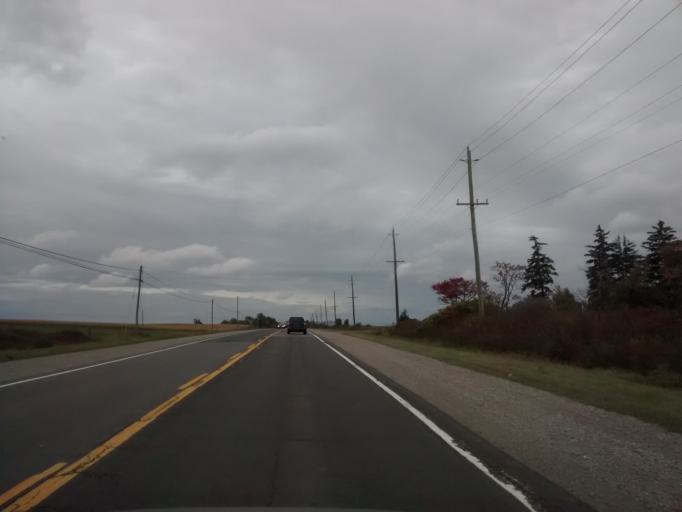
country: CA
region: Ontario
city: Ancaster
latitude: 43.0179
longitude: -80.0016
